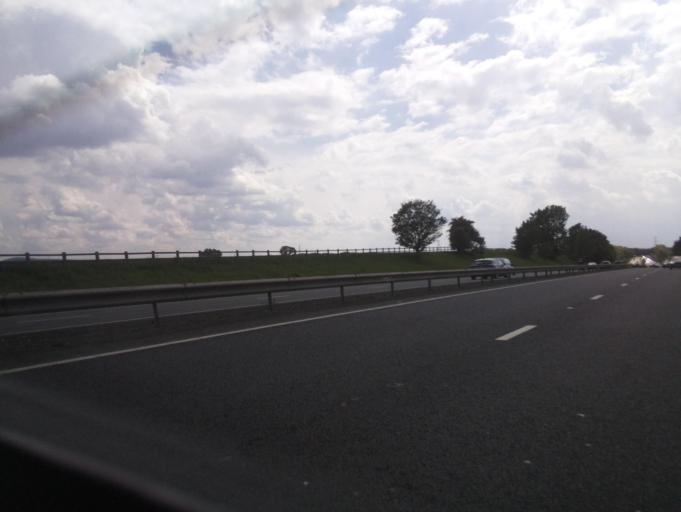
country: GB
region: England
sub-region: Redcar and Cleveland
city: Thornaby-on-Tees
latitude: 54.4950
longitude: -1.2980
